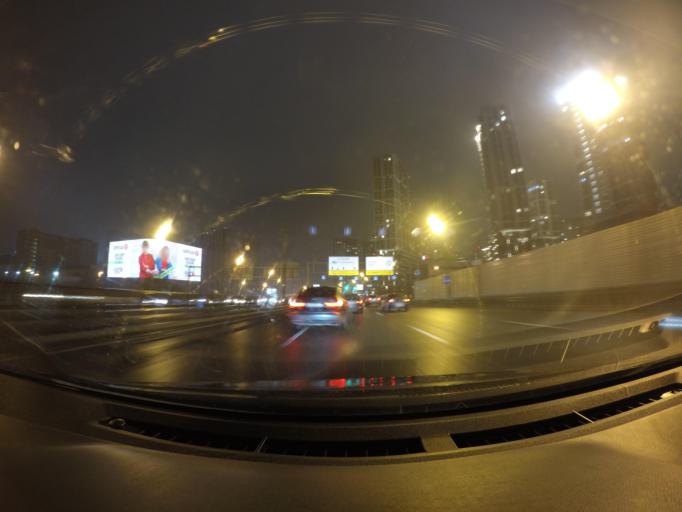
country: RU
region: Moscow
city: Lefortovo
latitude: 55.7483
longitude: 37.6993
